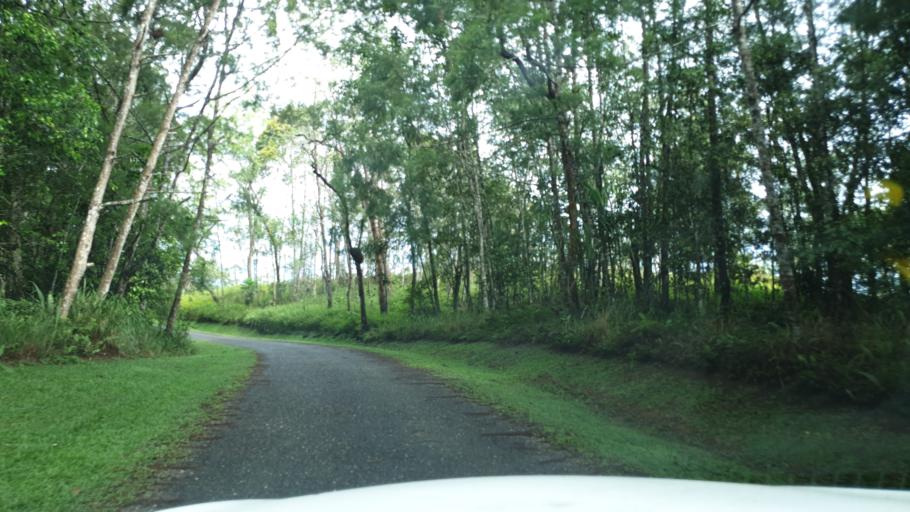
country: PG
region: National Capital
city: Port Moresby
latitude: -9.4332
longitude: 147.3722
